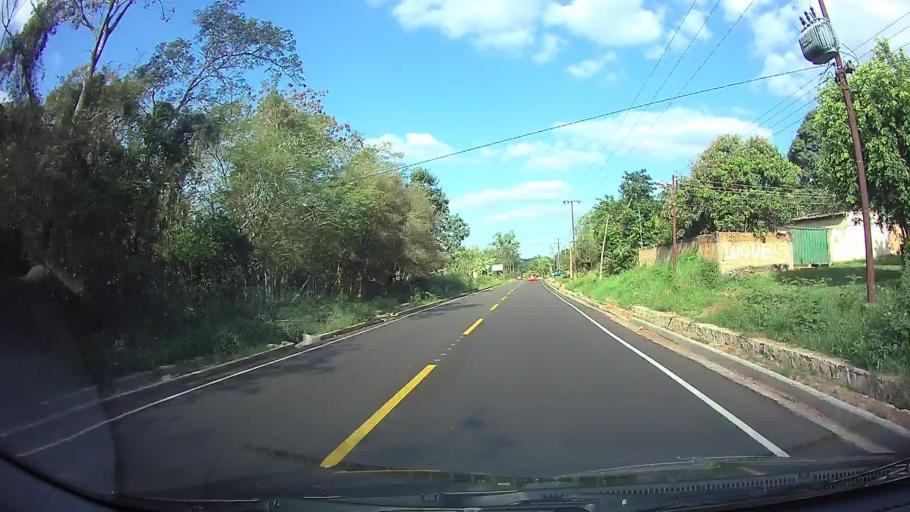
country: PY
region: Central
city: San Lorenzo
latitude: -25.2700
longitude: -57.4652
